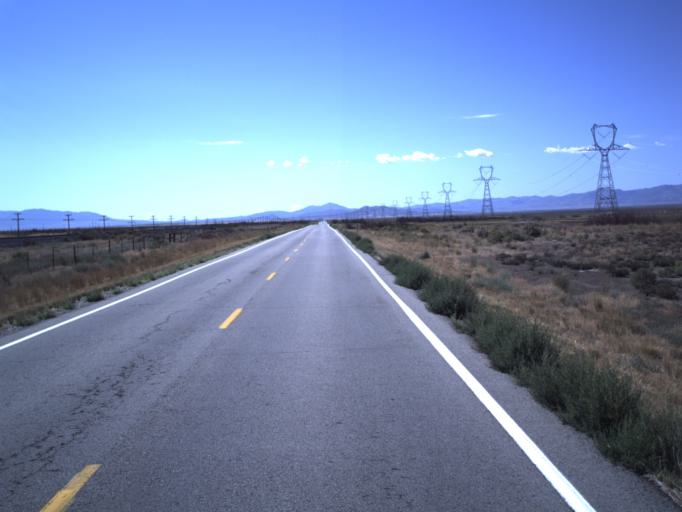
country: US
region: Utah
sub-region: Tooele County
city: Tooele
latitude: 40.3294
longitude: -112.4081
